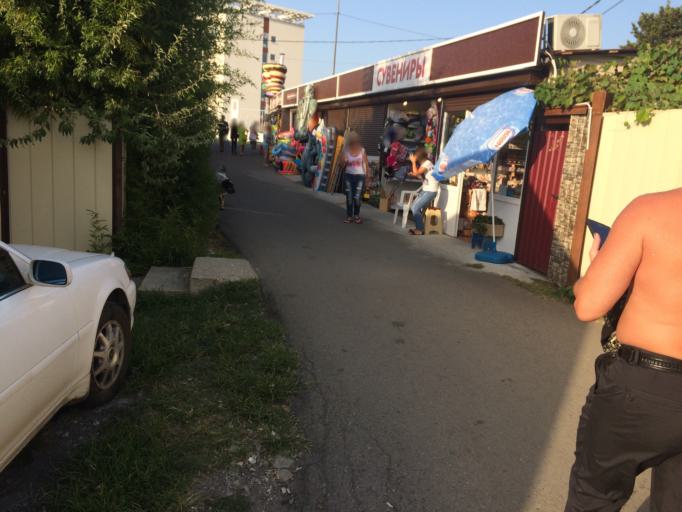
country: RU
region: Krasnodarskiy
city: Adler
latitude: 43.3876
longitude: 39.9895
